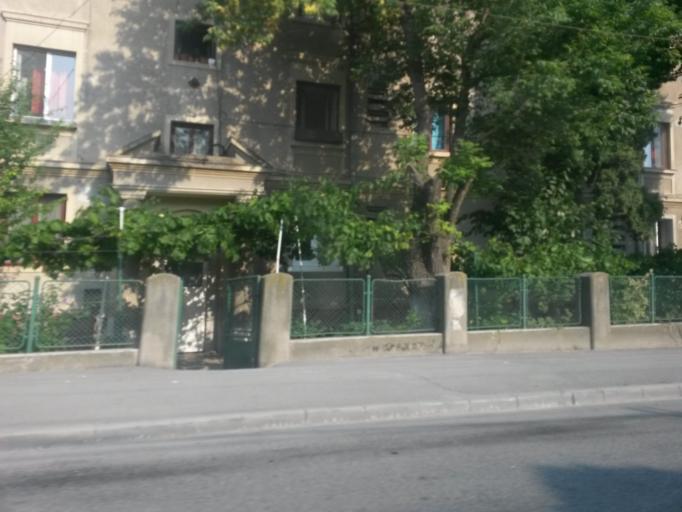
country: RO
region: Cluj
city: Turda
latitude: 46.5696
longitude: 23.7800
